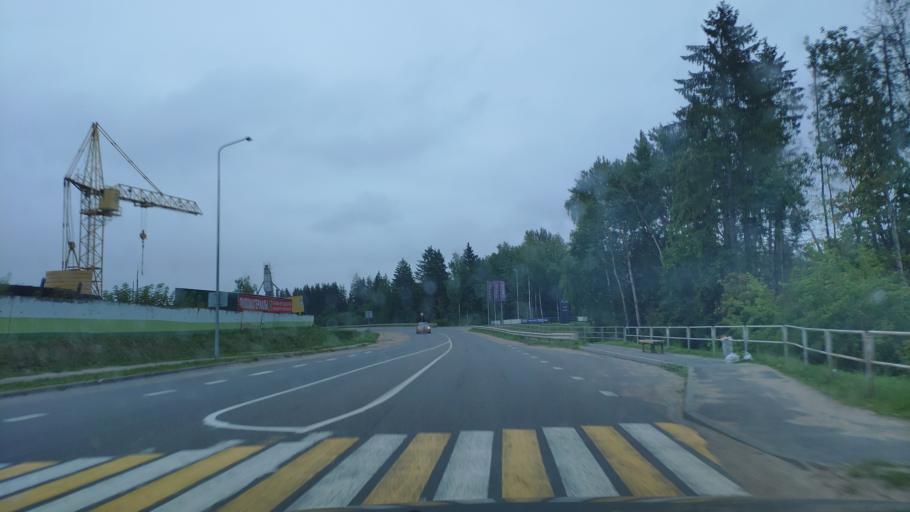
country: BY
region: Minsk
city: Azyartso
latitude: 53.8449
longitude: 27.4152
